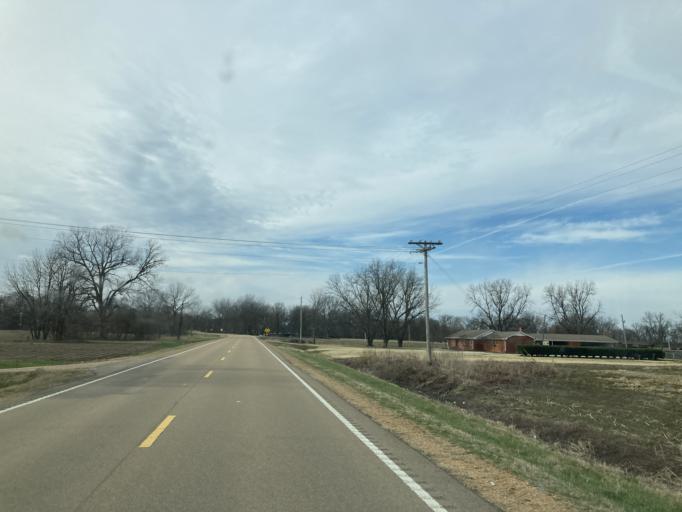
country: US
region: Mississippi
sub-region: Washington County
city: Hollandale
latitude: 33.1844
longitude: -90.6793
